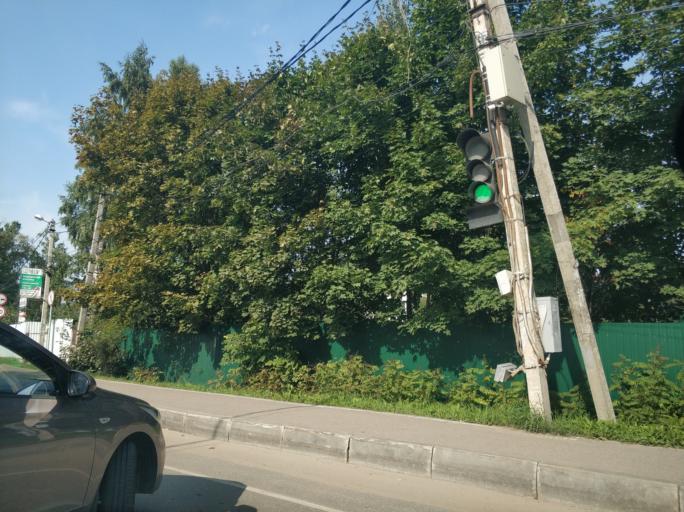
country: RU
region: Leningrad
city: Murino
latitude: 60.0471
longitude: 30.4611
